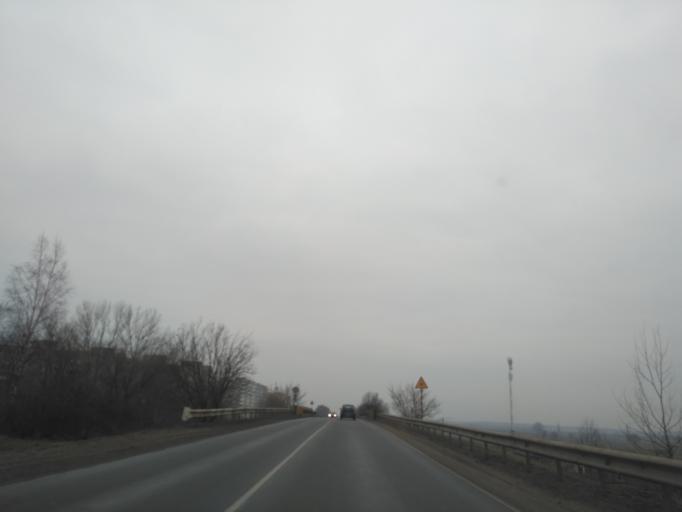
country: BY
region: Brest
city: Baranovichi
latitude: 53.1600
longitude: 26.0090
